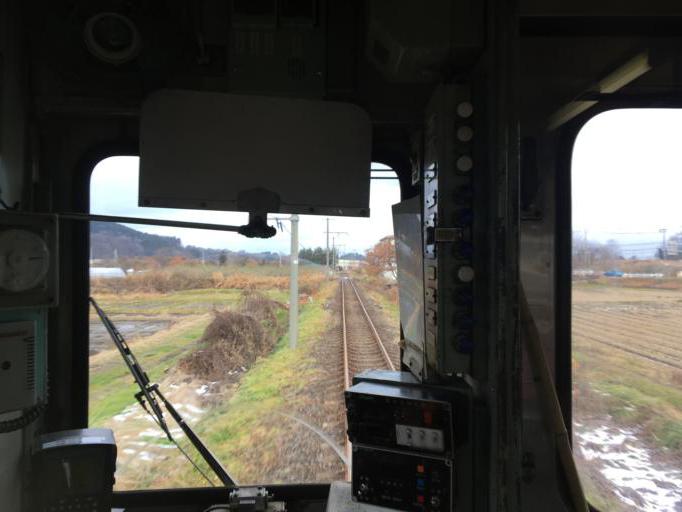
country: JP
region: Aomori
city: Hirosaki
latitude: 40.5279
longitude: 140.5559
